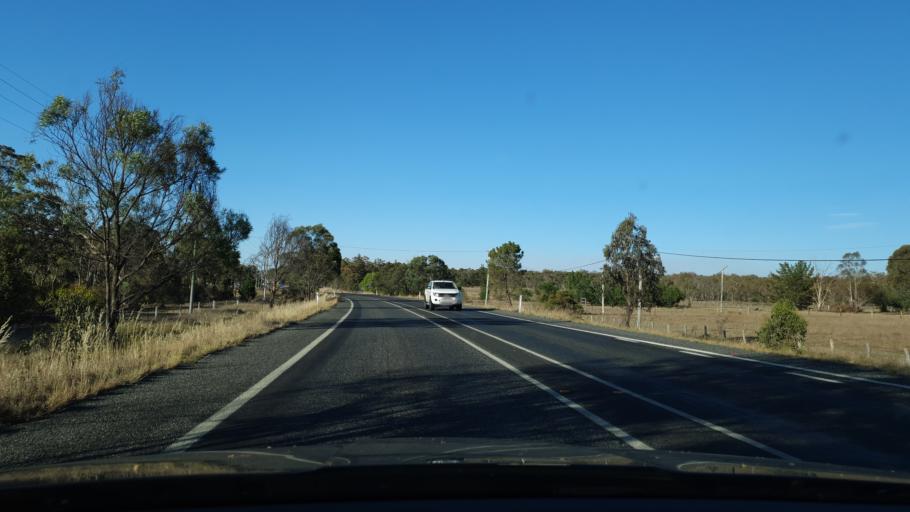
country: AU
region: Queensland
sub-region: Southern Downs
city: Stanthorpe
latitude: -28.7017
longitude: 151.9047
